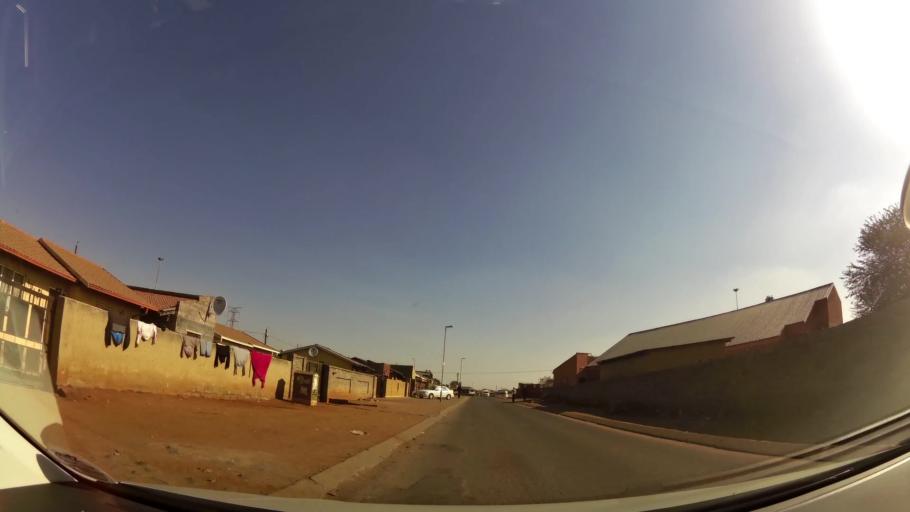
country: ZA
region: Gauteng
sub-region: City of Johannesburg Metropolitan Municipality
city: Soweto
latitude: -26.2871
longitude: 27.8685
